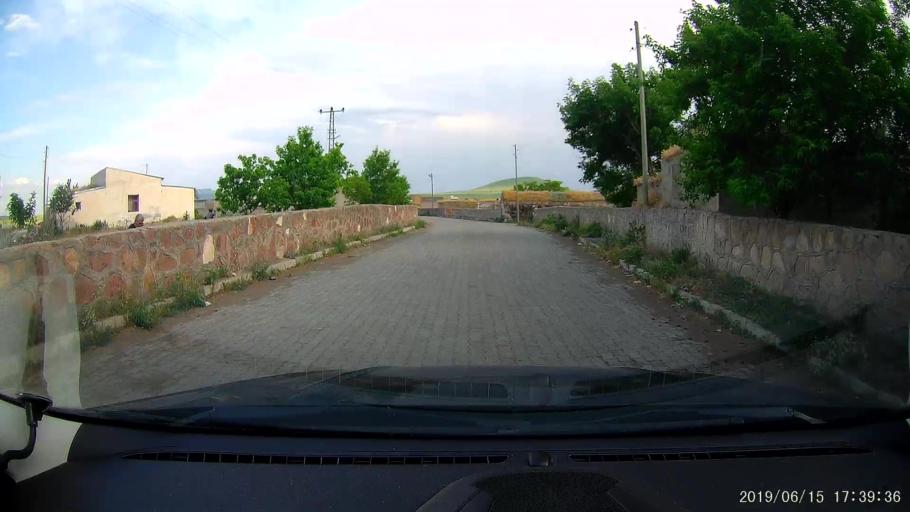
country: TR
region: Kars
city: Basgedikler
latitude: 40.5153
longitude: 43.5707
